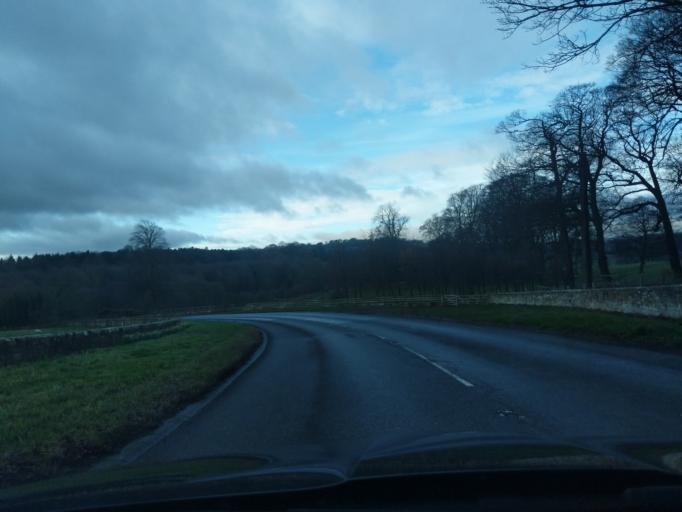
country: GB
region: England
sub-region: Northumberland
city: Alnwick
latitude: 55.4199
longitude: -1.6892
